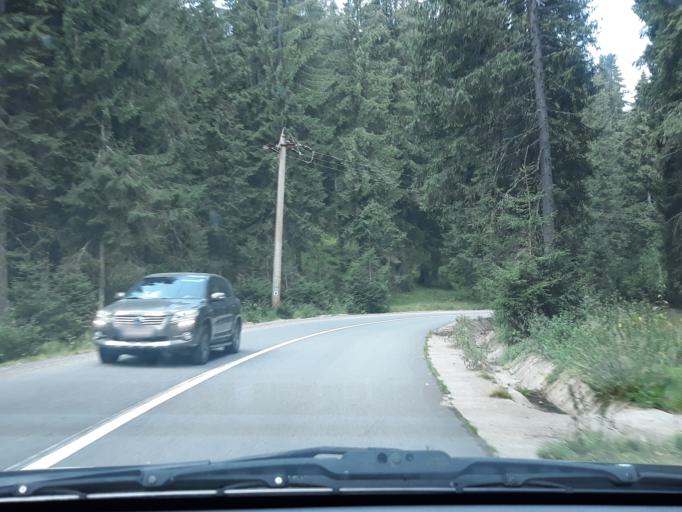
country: RO
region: Alba
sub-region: Comuna Arieseni
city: Arieseni
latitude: 46.5952
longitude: 22.7260
